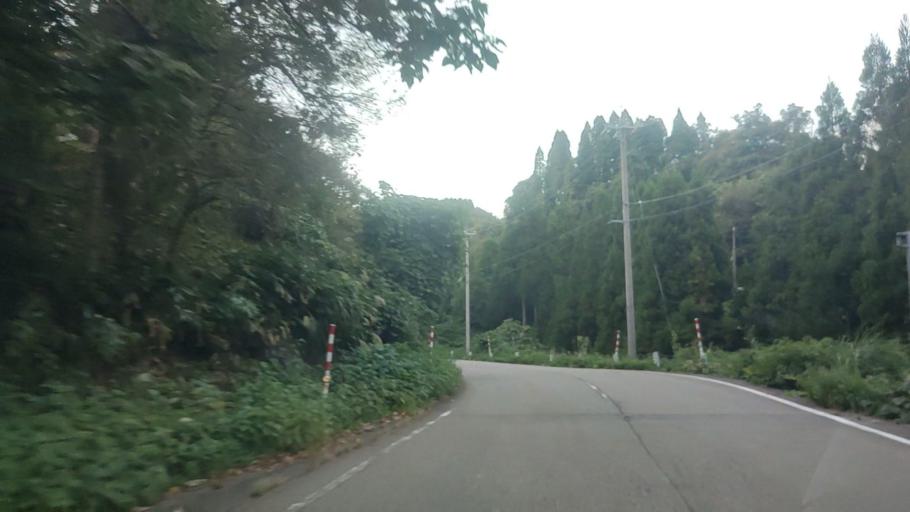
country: JP
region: Ishikawa
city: Tsubata
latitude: 36.6342
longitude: 136.7703
